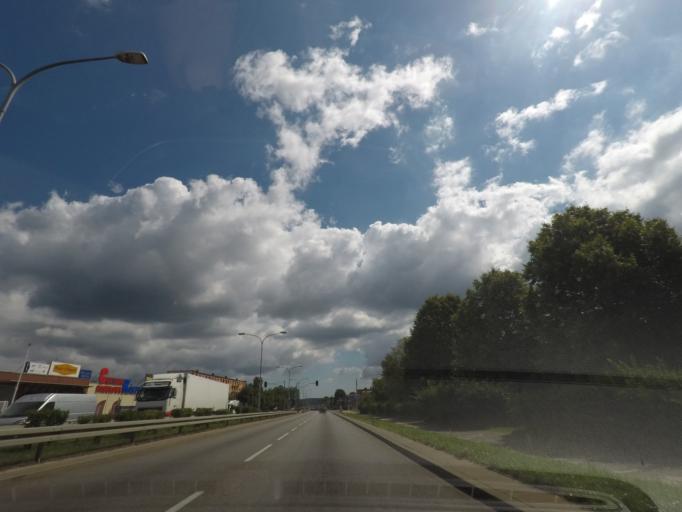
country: PL
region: Pomeranian Voivodeship
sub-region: Powiat wejherowski
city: Wejherowo
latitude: 54.6039
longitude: 18.2509
